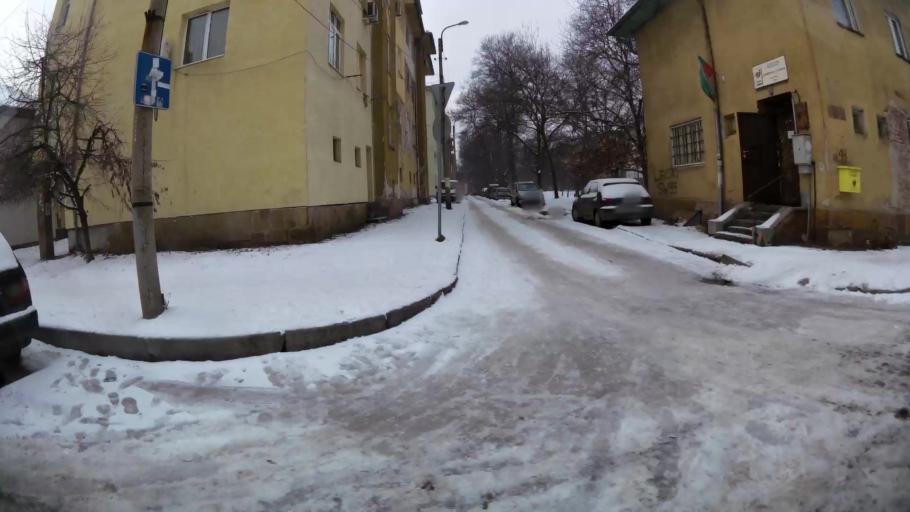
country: BG
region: Sofia-Capital
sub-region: Stolichna Obshtina
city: Sofia
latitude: 42.7157
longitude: 23.2879
